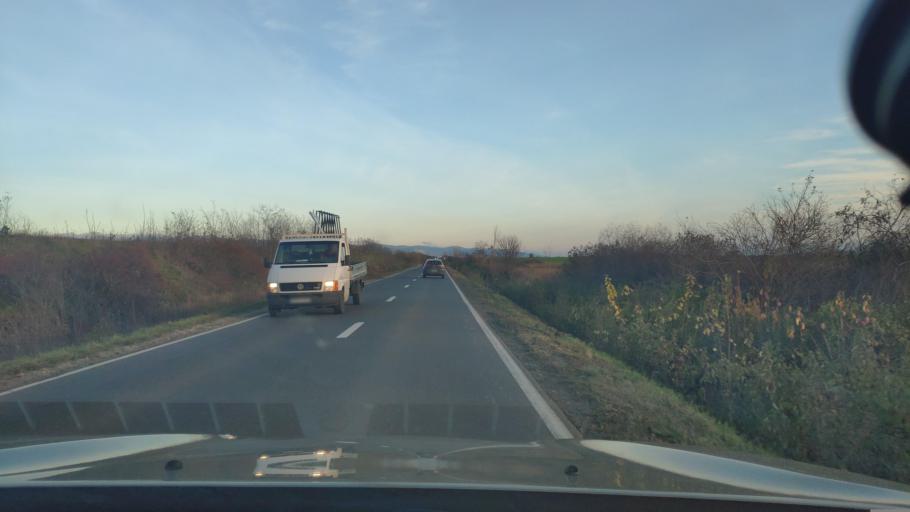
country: RO
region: Satu Mare
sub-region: Comuna Mediesu Aurit
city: Mediesu Aurit
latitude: 47.7704
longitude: 23.1445
